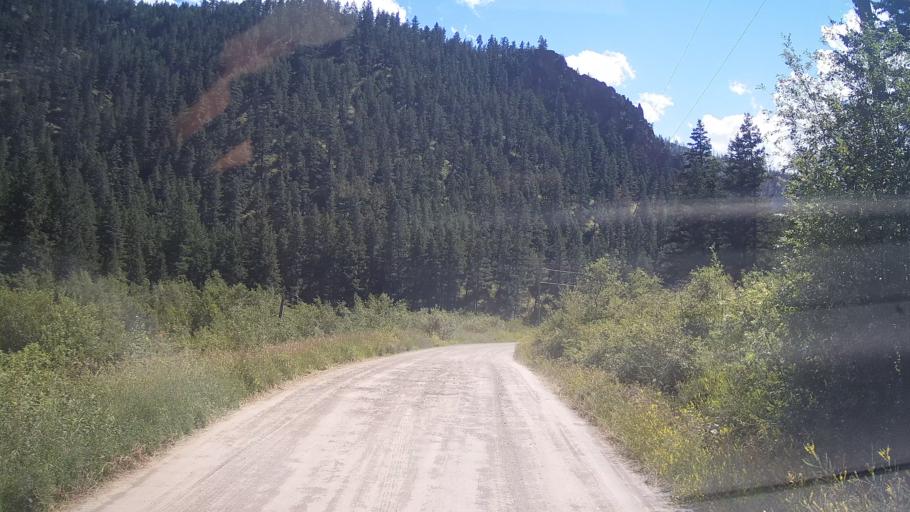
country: CA
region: British Columbia
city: Lillooet
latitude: 51.2338
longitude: -122.0520
